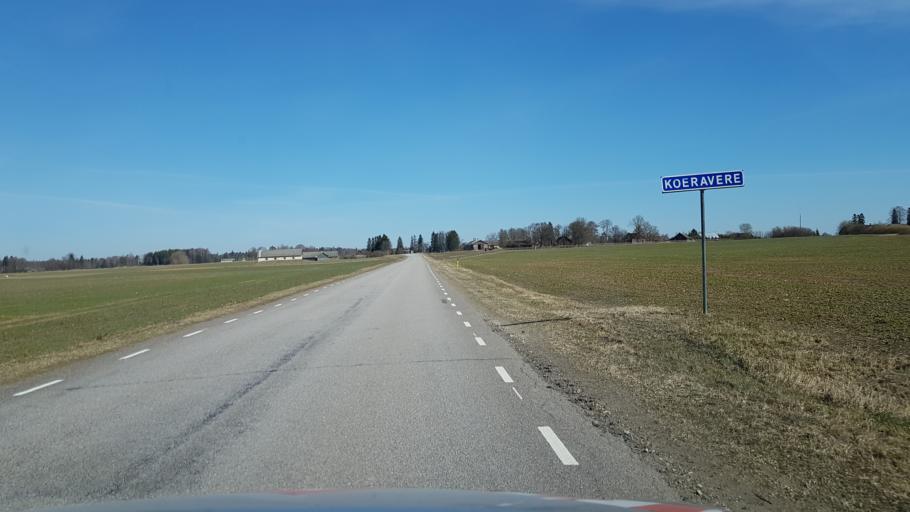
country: EE
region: Laeaene-Virumaa
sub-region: Vinni vald
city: Vinni
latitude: 59.2469
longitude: 26.3542
